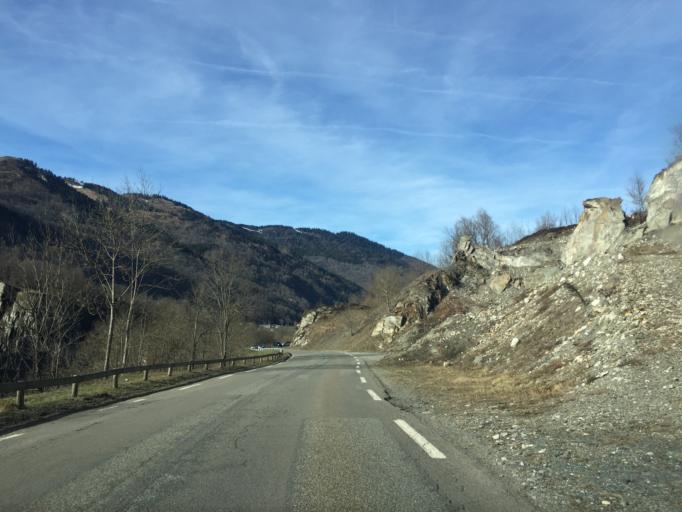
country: FR
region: Midi-Pyrenees
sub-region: Departement des Hautes-Pyrenees
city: Saint-Lary-Soulan
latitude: 42.8087
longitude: 0.4103
